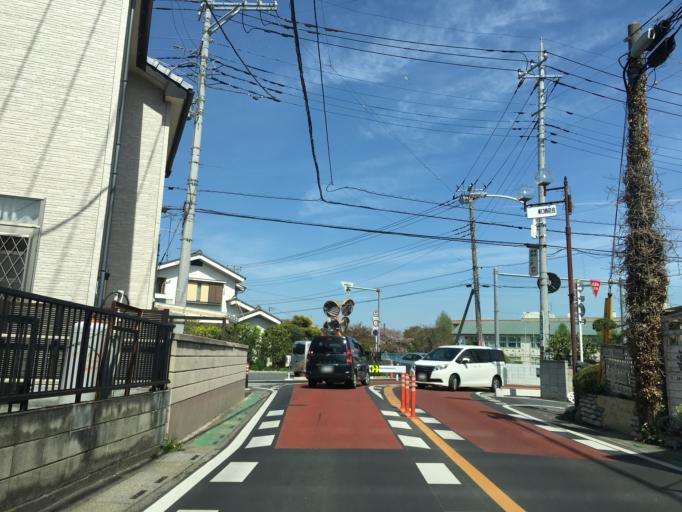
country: JP
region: Saitama
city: Sugito
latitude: 36.0218
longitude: 139.7325
